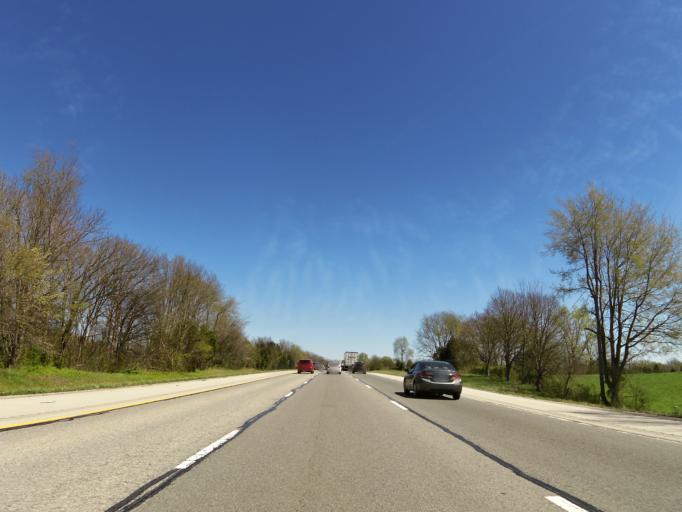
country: US
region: Kentucky
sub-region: Warren County
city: Bowling Green
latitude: 37.0158
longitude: -86.2784
